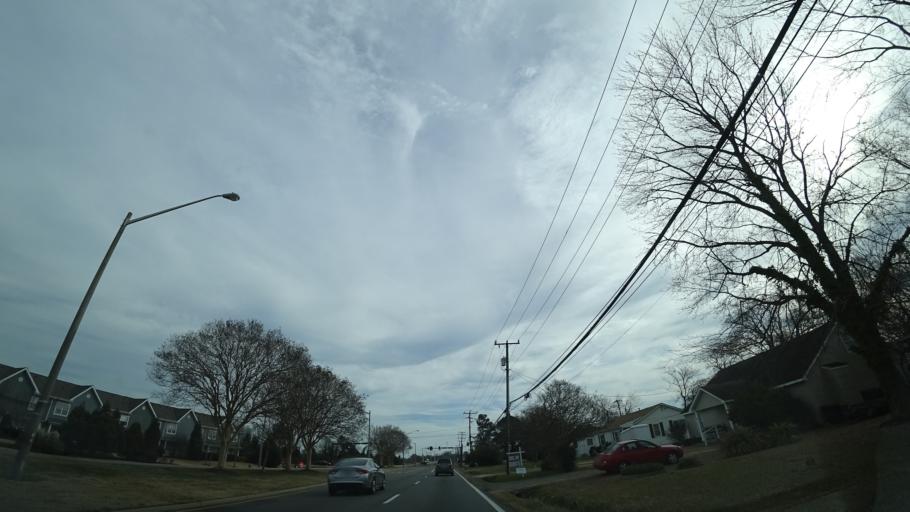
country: US
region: Virginia
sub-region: City of Hampton
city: Hampton
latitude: 37.0381
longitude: -76.3707
